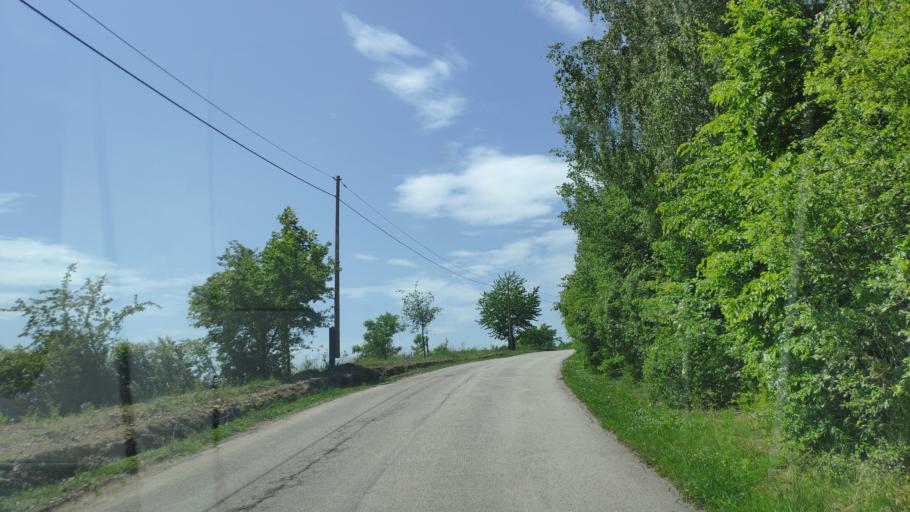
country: SK
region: Kosicky
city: Medzev
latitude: 48.7154
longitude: 20.9830
